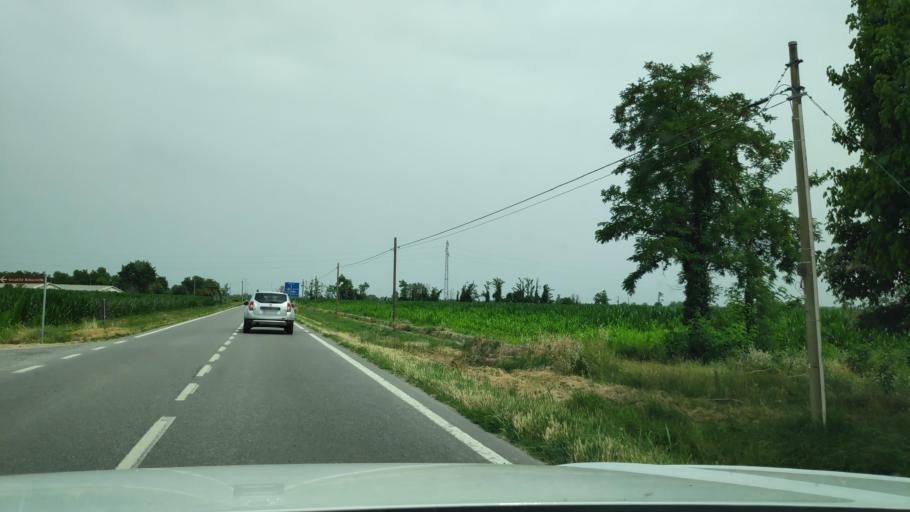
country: IT
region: Lombardy
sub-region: Provincia di Cremona
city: Casaletto di Sopra
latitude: 45.4149
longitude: 9.7711
